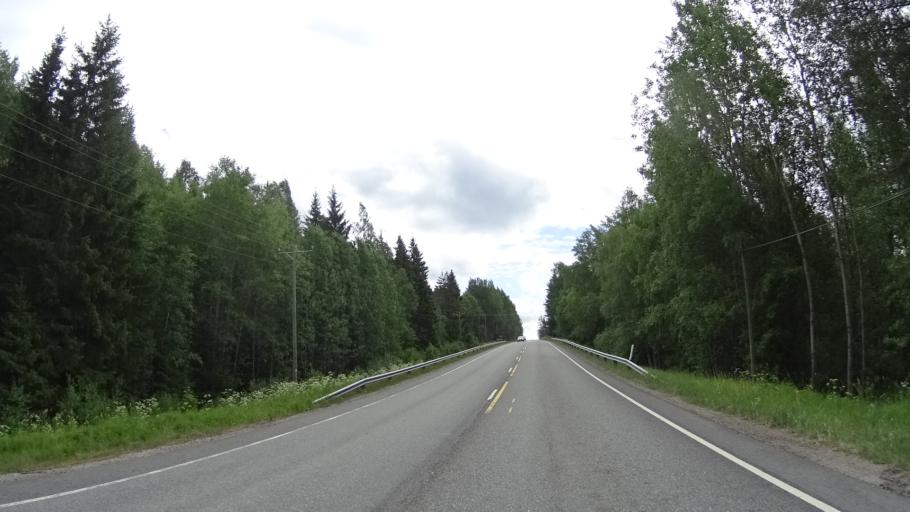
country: FI
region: Uusimaa
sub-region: Helsinki
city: Vihti
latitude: 60.2960
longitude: 24.3876
